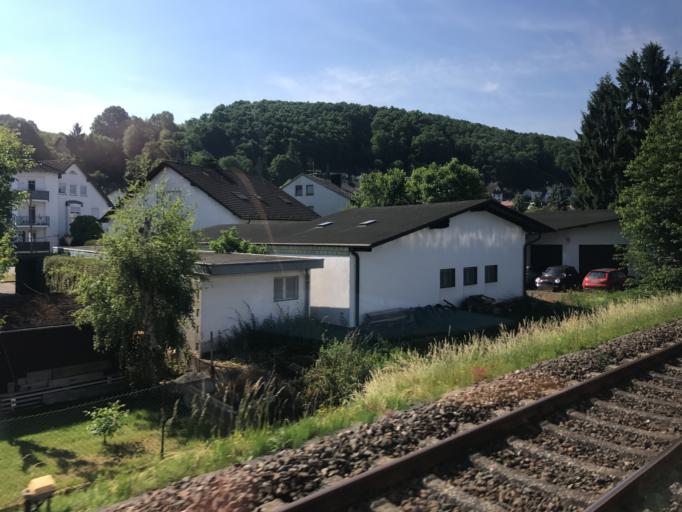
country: DE
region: Rheinland-Pfalz
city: Fischbach
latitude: 49.7264
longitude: 7.3908
